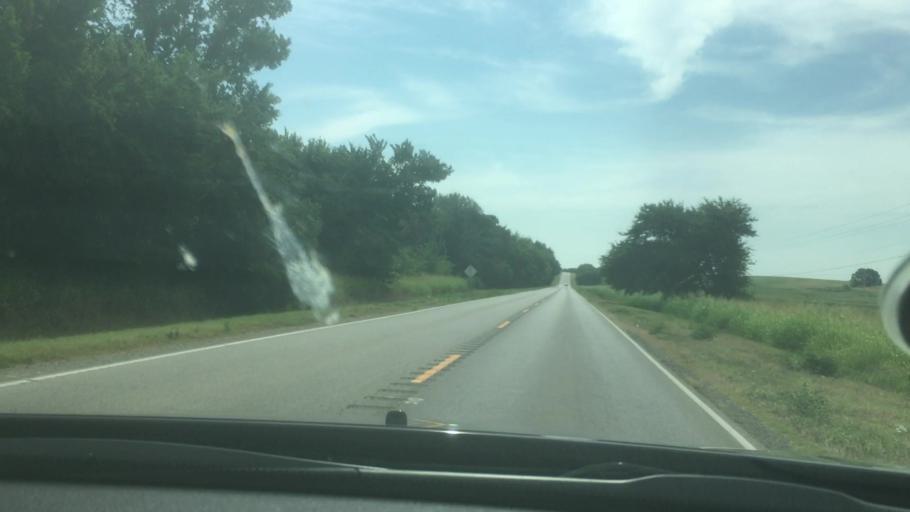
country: US
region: Oklahoma
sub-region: Garvin County
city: Maysville
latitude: 34.8148
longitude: -97.3913
